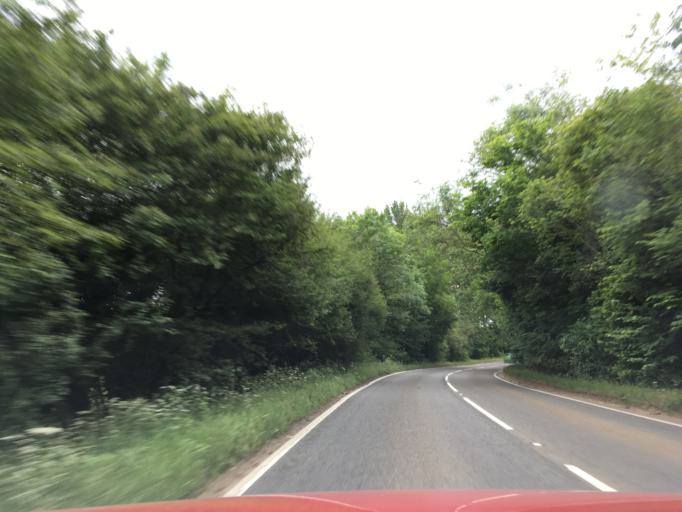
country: GB
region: England
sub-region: Central Bedfordshire
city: Potsgrove
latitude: 51.9596
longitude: -0.6424
